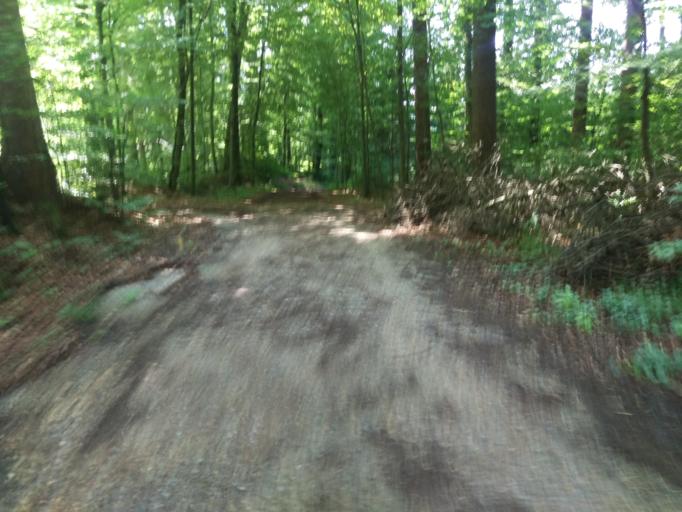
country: AT
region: Styria
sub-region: Graz Stadt
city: Mariatrost
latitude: 47.1222
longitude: 15.5039
